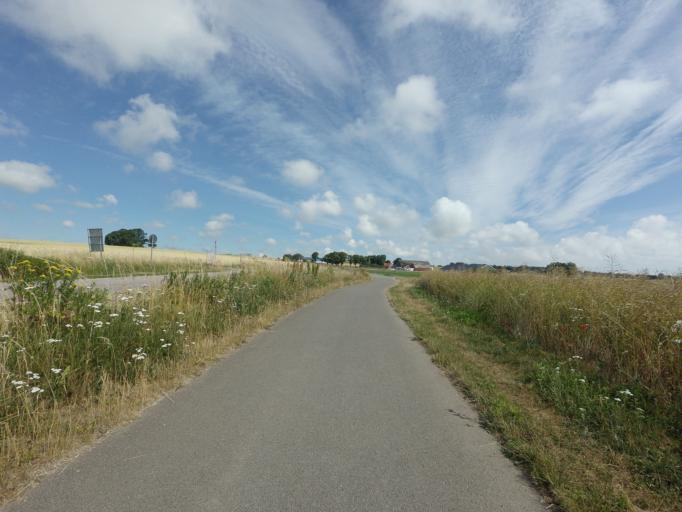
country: SE
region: Skane
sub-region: Simrishamns Kommun
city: Simrishamn
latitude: 55.4805
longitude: 14.2846
